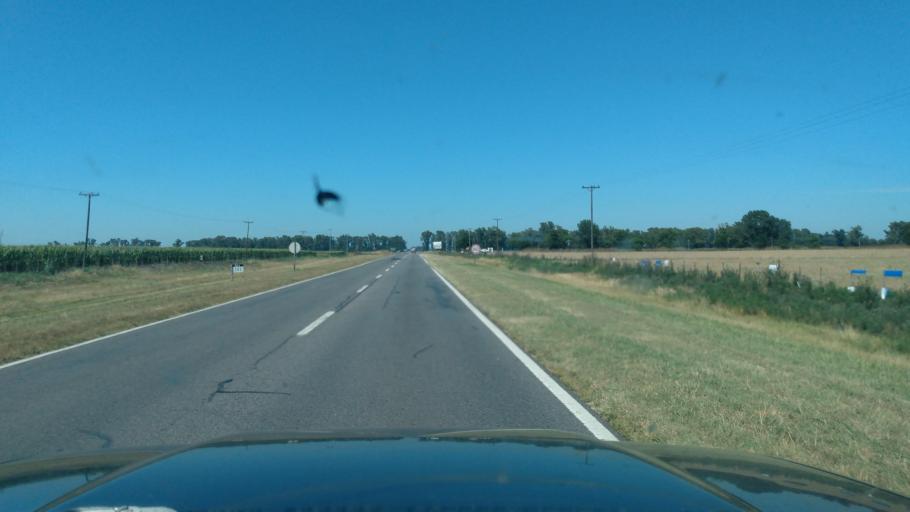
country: AR
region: Buenos Aires
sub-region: Partido de Bragado
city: Bragado
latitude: -35.0890
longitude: -60.3908
